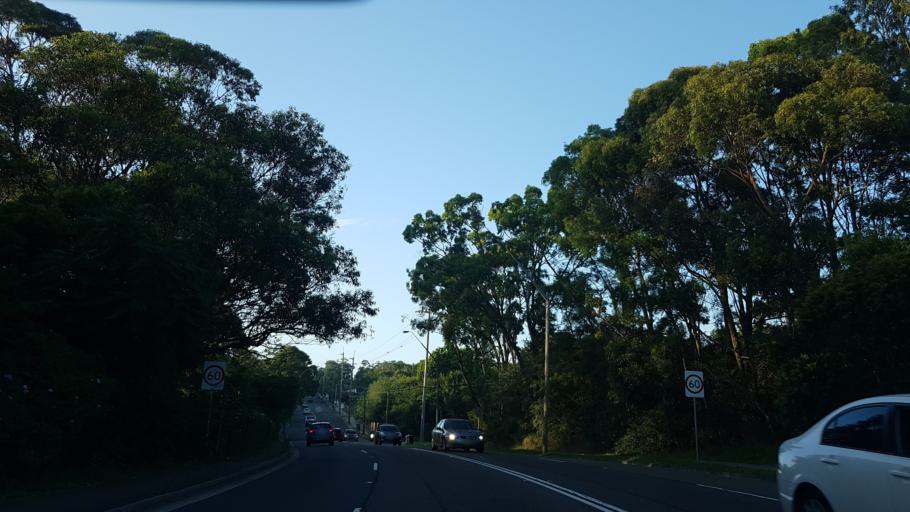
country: AU
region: New South Wales
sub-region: Warringah
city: Narraweena
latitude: -33.7482
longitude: 151.2622
